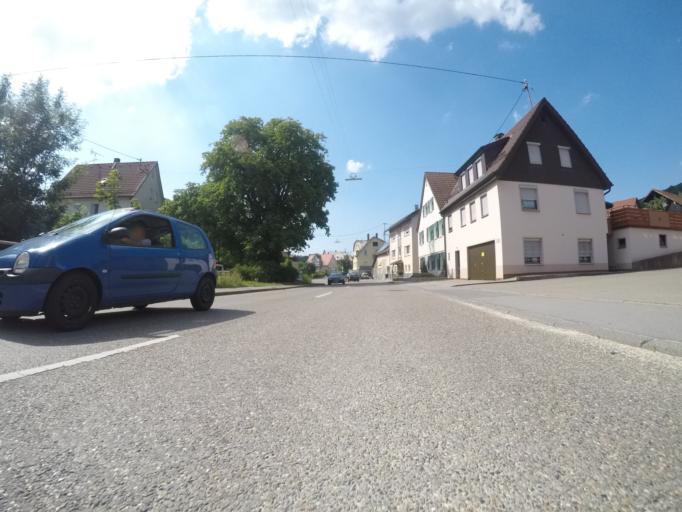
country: DE
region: Baden-Wuerttemberg
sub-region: Regierungsbezirk Stuttgart
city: Owen
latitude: 48.5638
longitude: 9.4615
